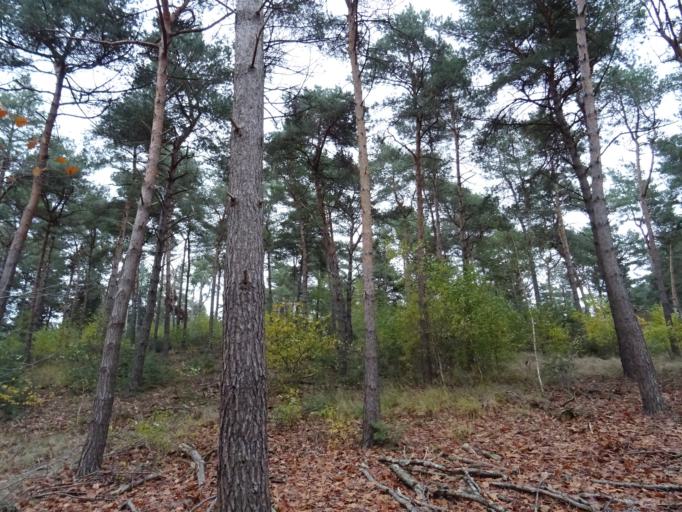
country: NL
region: Limburg
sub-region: Gemeente Roerdalen
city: Herkenbosch
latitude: 51.2134
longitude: 6.0709
